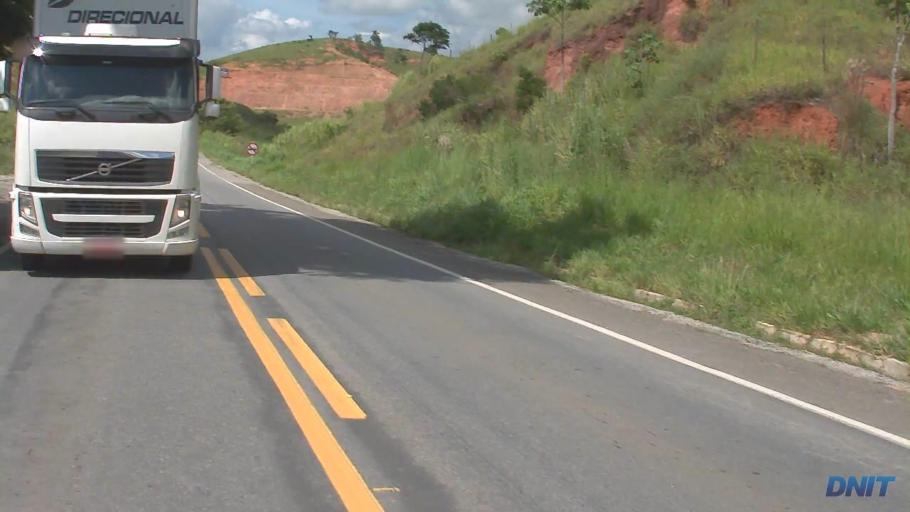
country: BR
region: Minas Gerais
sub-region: Governador Valadares
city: Governador Valadares
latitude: -19.0377
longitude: -42.1480
